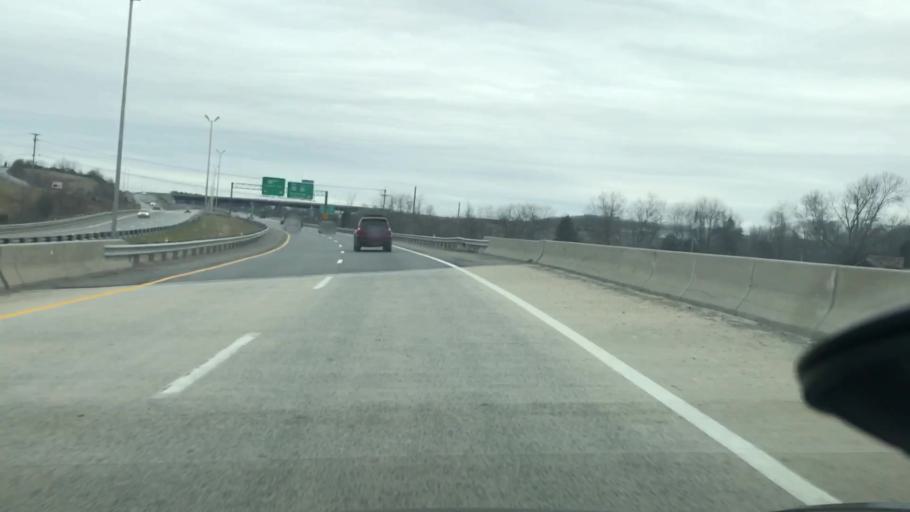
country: US
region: Virginia
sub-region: Montgomery County
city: Merrimac
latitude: 37.1839
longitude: -80.4028
